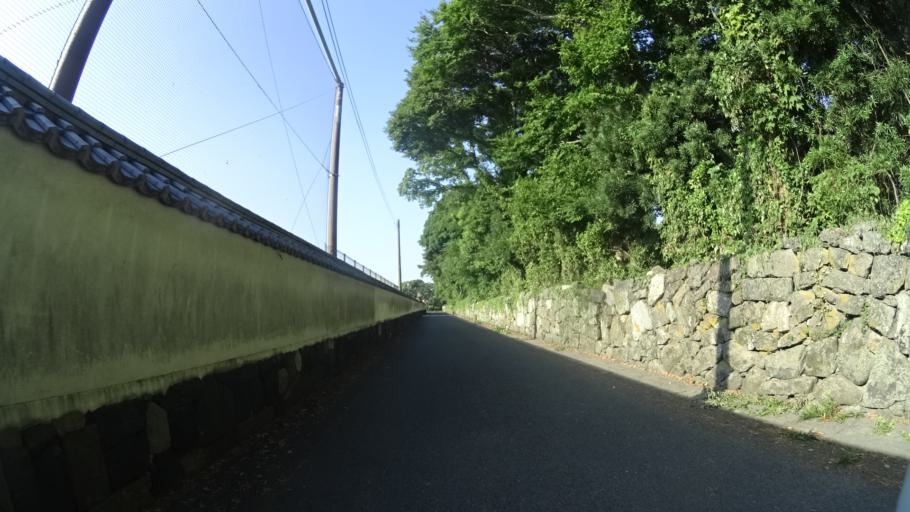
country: JP
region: Yamaguchi
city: Hagi
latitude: 34.4137
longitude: 131.3843
